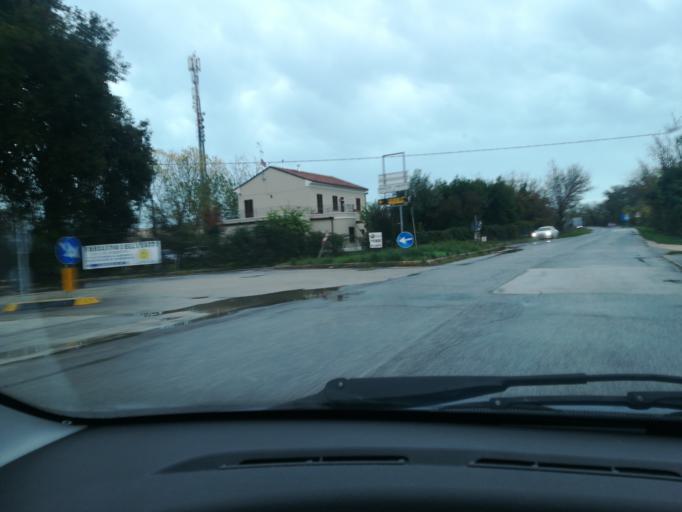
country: IT
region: The Marches
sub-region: Provincia di Macerata
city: Trodica
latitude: 43.2775
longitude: 13.6129
